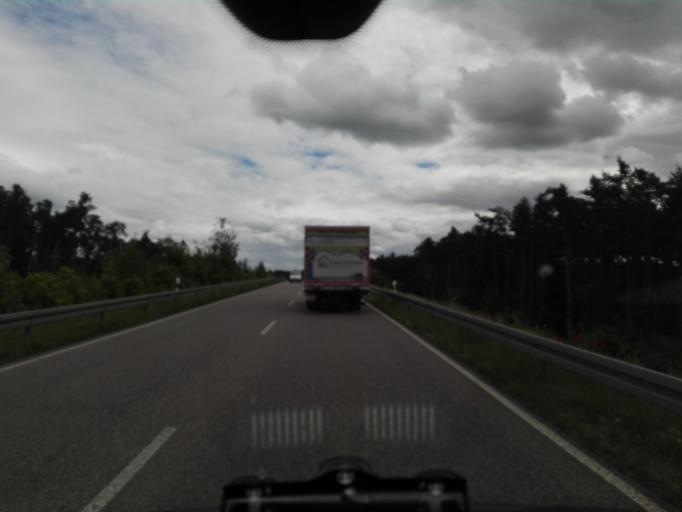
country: DE
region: Baden-Wuerttemberg
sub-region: Karlsruhe Region
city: Graben-Neudorf
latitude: 49.1399
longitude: 8.4822
